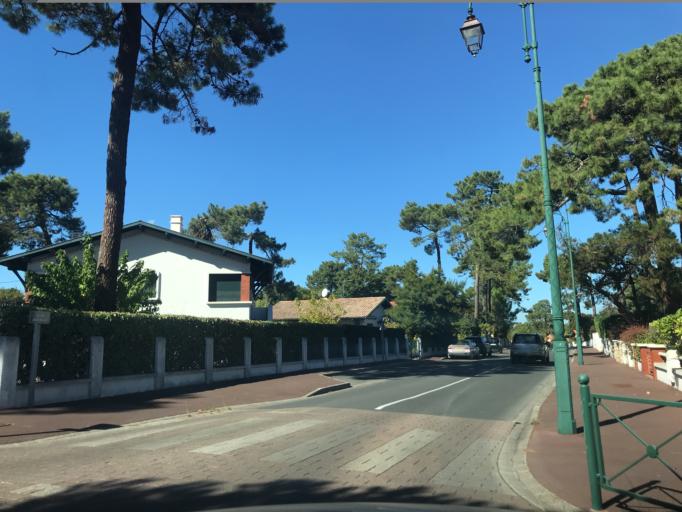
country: FR
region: Aquitaine
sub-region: Departement de la Gironde
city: Arcachon
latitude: 44.6499
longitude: -1.1795
